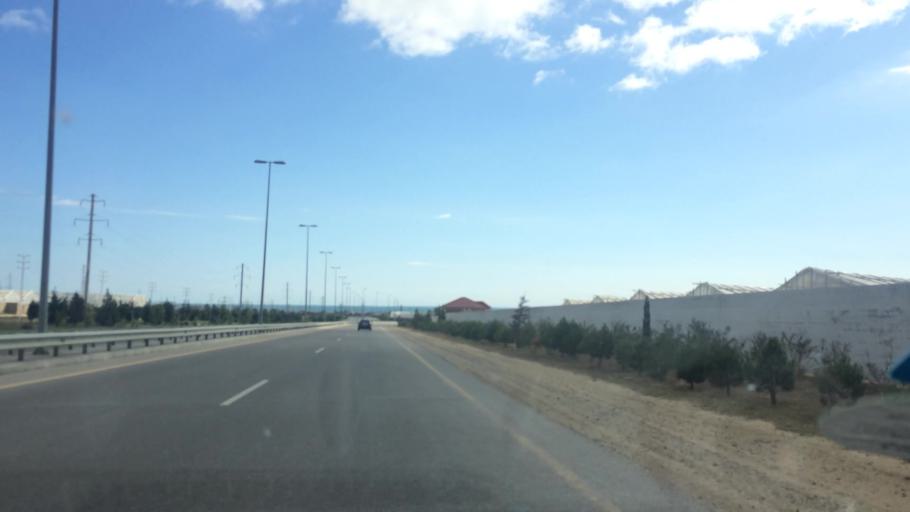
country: AZ
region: Baki
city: Zyrya
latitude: 40.4000
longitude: 50.3159
